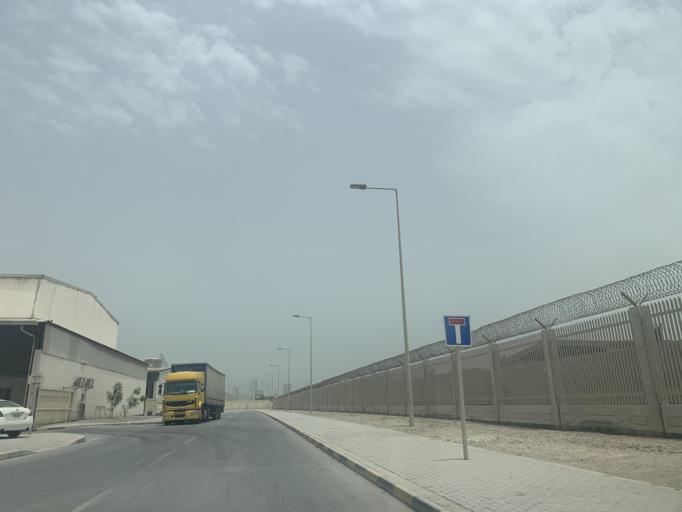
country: BH
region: Northern
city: Sitrah
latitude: 26.1829
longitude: 50.6191
